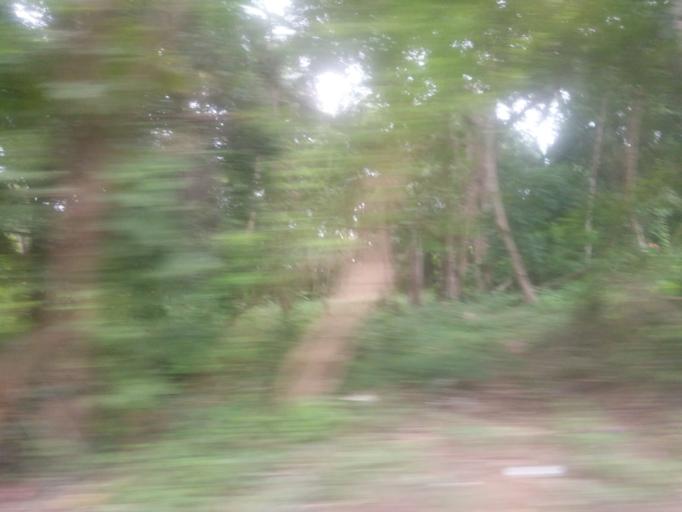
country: IN
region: Goa
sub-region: South Goa
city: Varca
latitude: 15.2144
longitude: 73.9501
